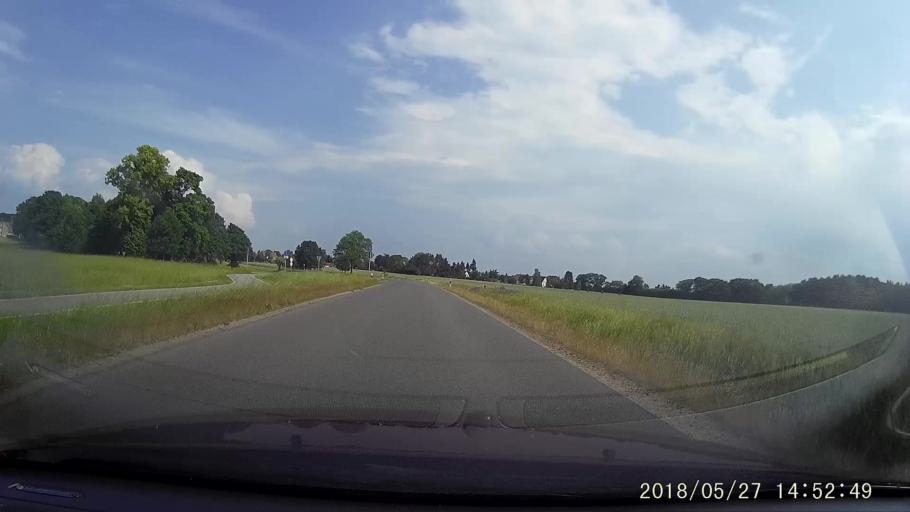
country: DE
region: Saxony
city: Klitten
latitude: 51.3534
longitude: 14.5854
